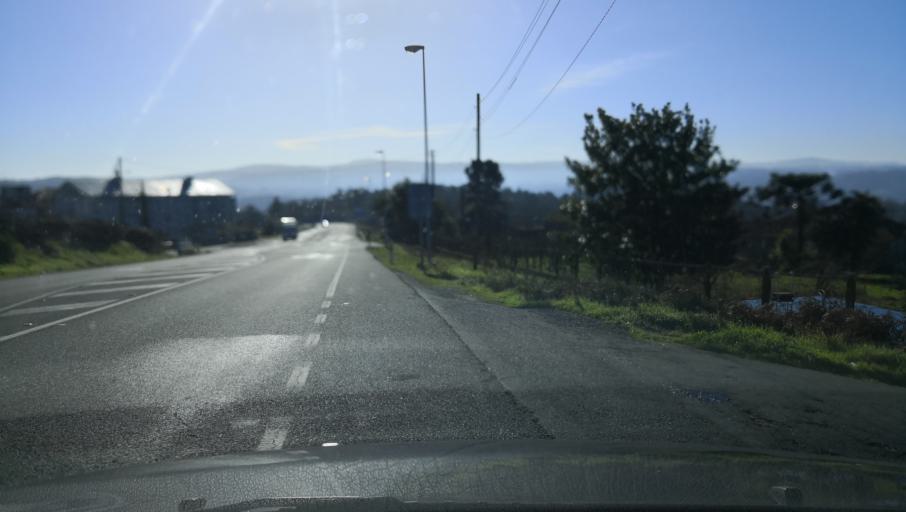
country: ES
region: Galicia
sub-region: Provincia da Coruna
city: Ribeira
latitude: 42.7781
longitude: -8.4274
